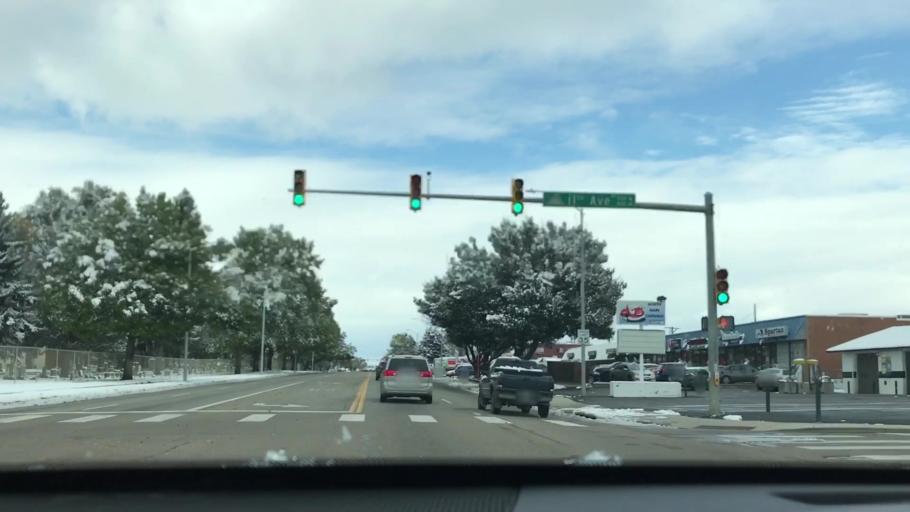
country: US
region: Colorado
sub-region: Boulder County
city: Longmont
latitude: 40.1775
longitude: -105.1024
